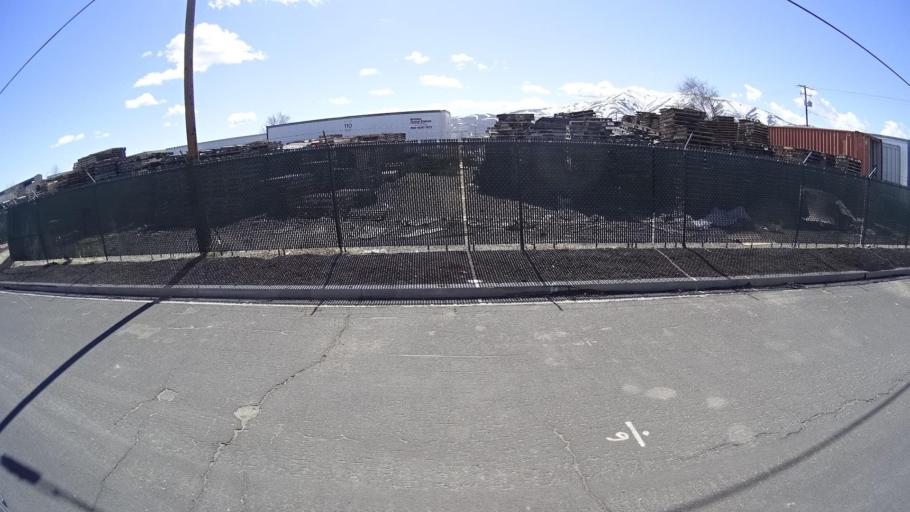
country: US
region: Nevada
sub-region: Washoe County
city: Lemmon Valley
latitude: 39.6545
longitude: -119.8848
